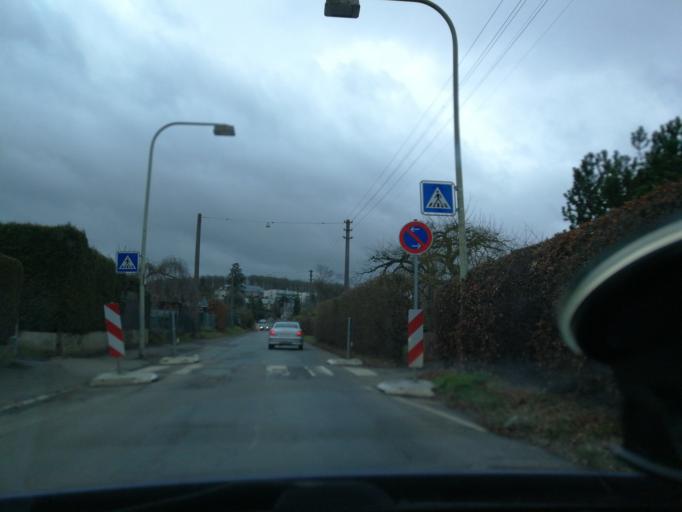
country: DE
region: Rheinland-Pfalz
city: Trier
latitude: 49.7279
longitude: 6.6386
